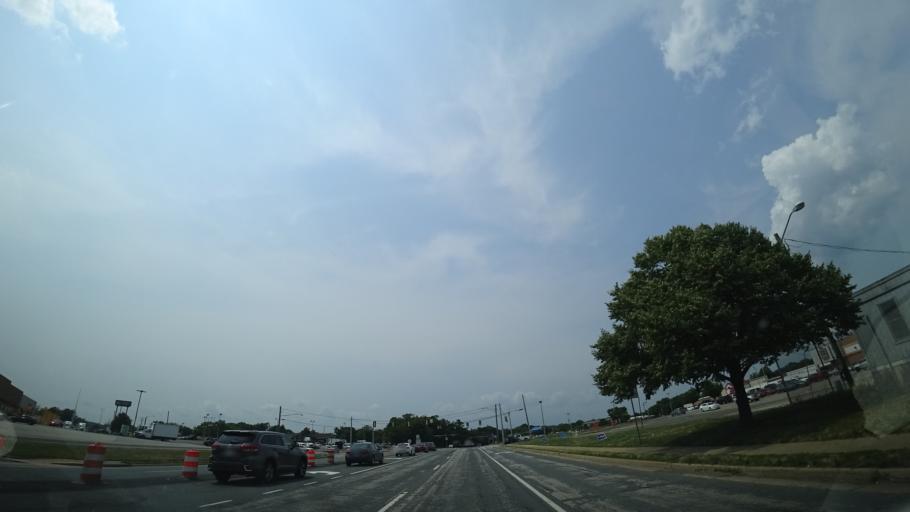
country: US
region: Virginia
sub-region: Prince William County
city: Woodbridge
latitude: 38.6629
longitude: -77.2484
